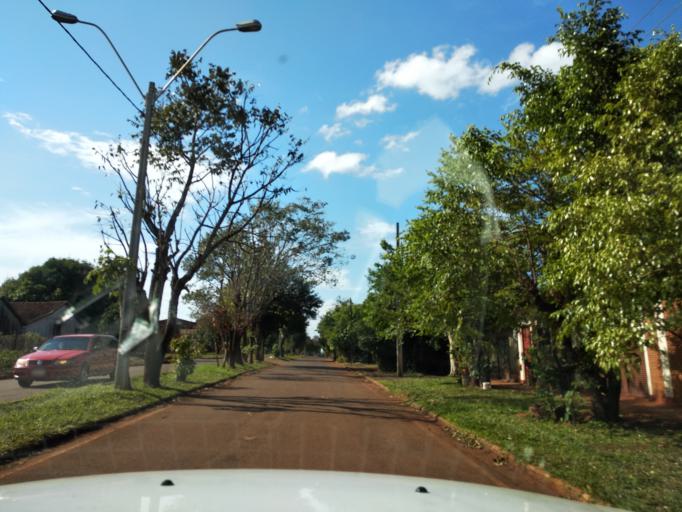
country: PY
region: Itapua
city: Hohenau
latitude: -27.0588
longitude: -55.7446
